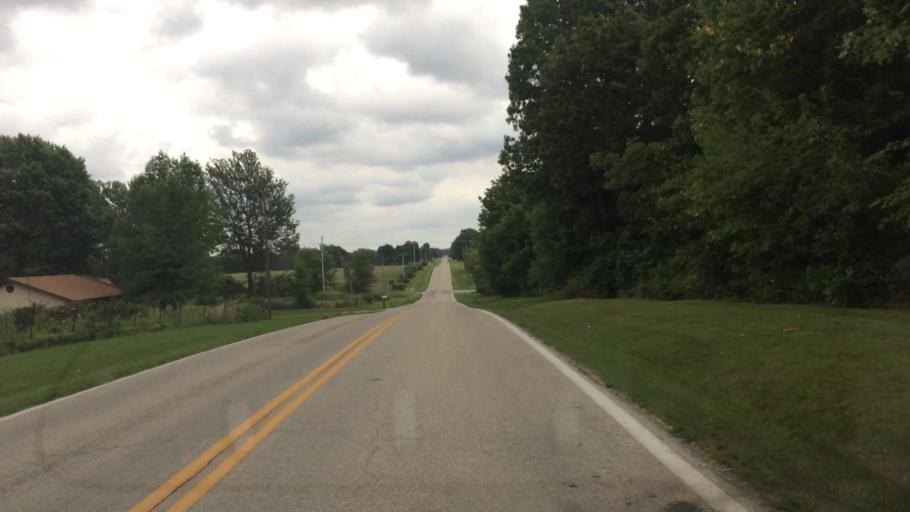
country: US
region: Missouri
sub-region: Greene County
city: Strafford
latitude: 37.3002
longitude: -93.1514
